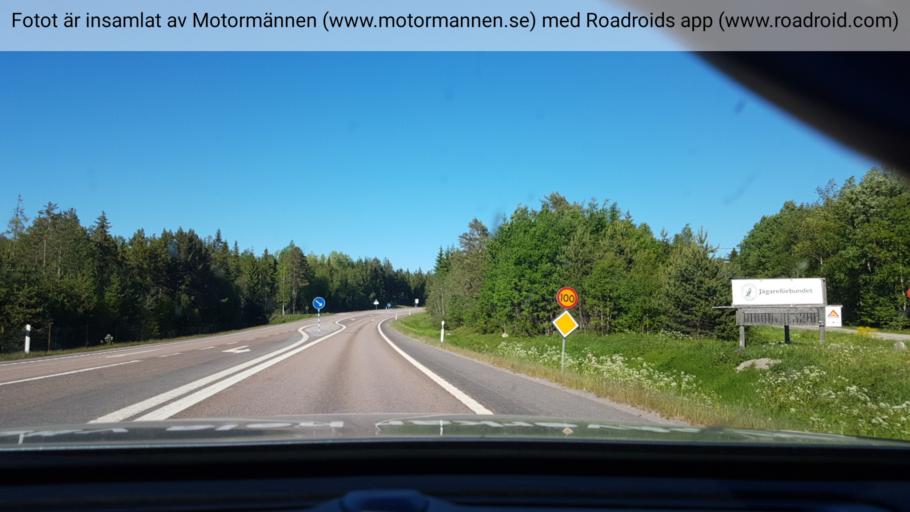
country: SE
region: Vaesternorrland
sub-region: Timra Kommun
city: Soraker
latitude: 62.5562
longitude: 17.6431
